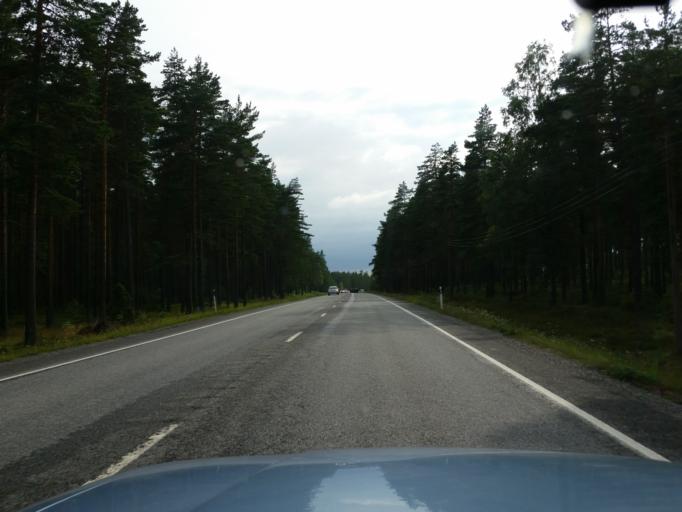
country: FI
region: Uusimaa
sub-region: Raaseporin
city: Pohja
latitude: 60.0235
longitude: 23.5777
